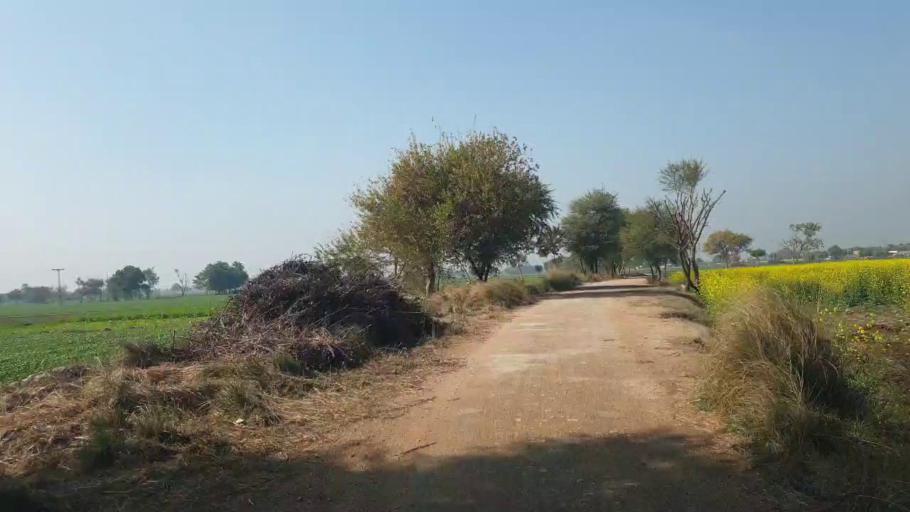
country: PK
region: Sindh
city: Shahdadpur
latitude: 25.9495
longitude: 68.5430
